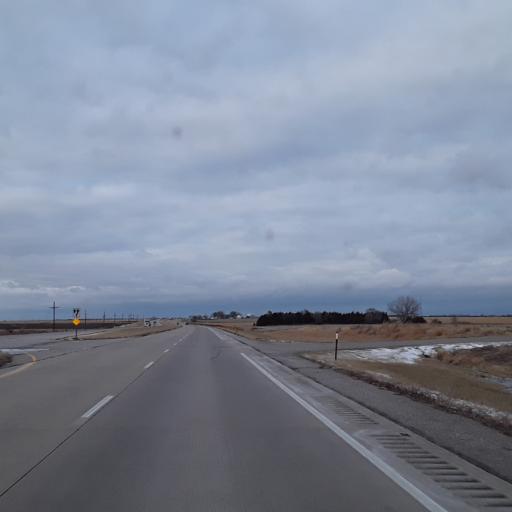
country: US
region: Nebraska
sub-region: Thayer County
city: Hebron
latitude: 40.3426
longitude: -97.5767
